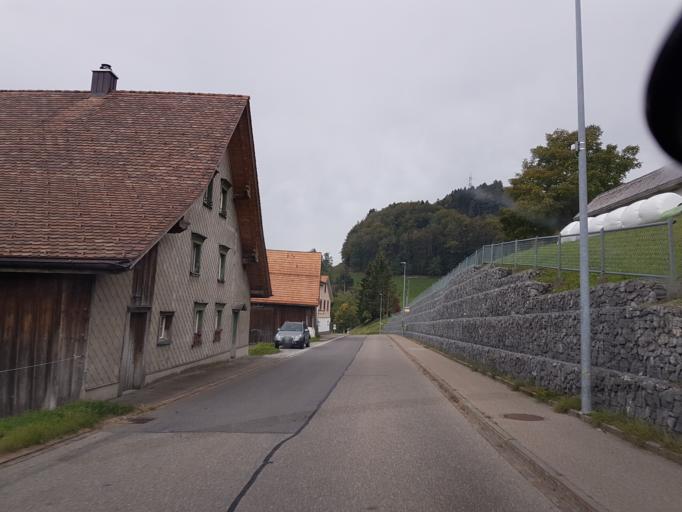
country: CH
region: Saint Gallen
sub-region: Wahlkreis See-Gaster
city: Goldingen
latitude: 47.2775
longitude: 8.9762
